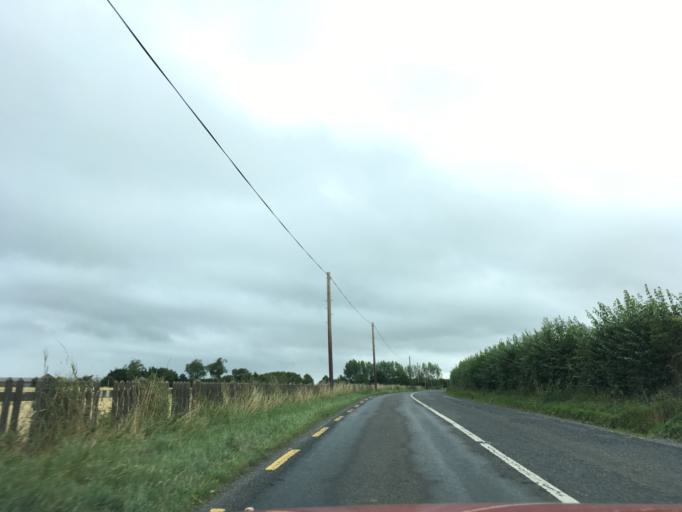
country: IE
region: Munster
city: Cashel
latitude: 52.4474
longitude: -7.8078
